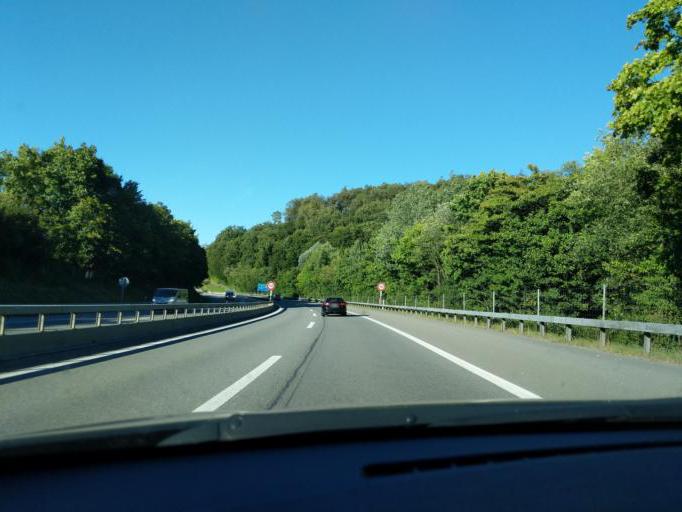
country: CH
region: Bern
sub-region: Bern-Mittelland District
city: Koniz
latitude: 46.9333
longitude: 7.3943
